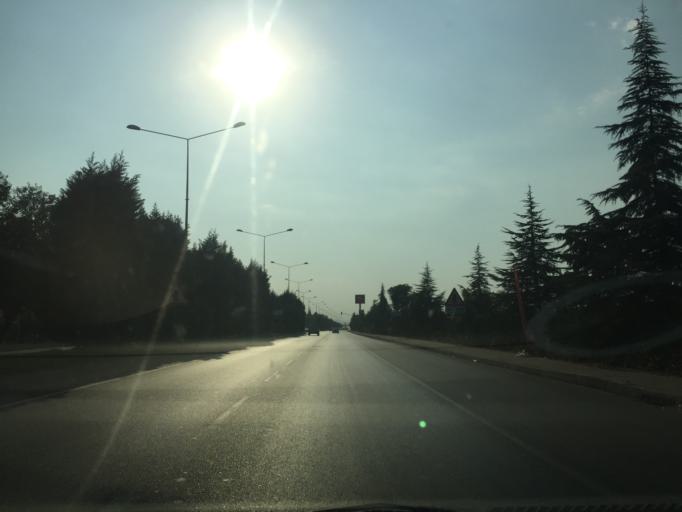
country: TR
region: Manisa
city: Salihli
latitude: 38.4894
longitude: 28.1540
